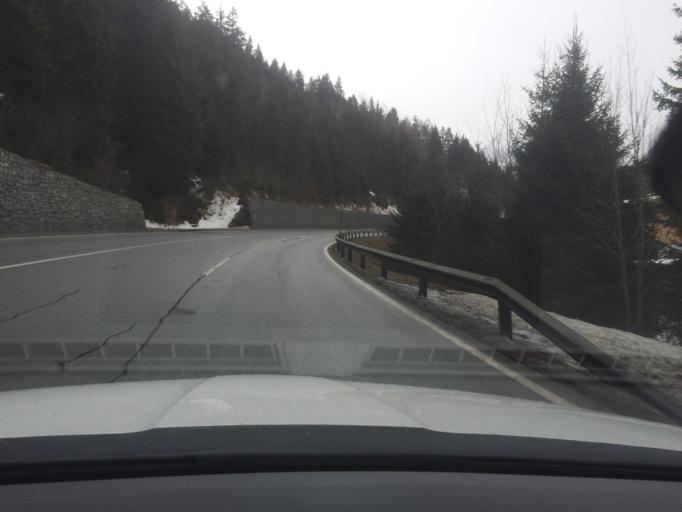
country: AT
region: Salzburg
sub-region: Politischer Bezirk Zell am See
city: Mittersill
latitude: 47.2513
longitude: 12.4881
